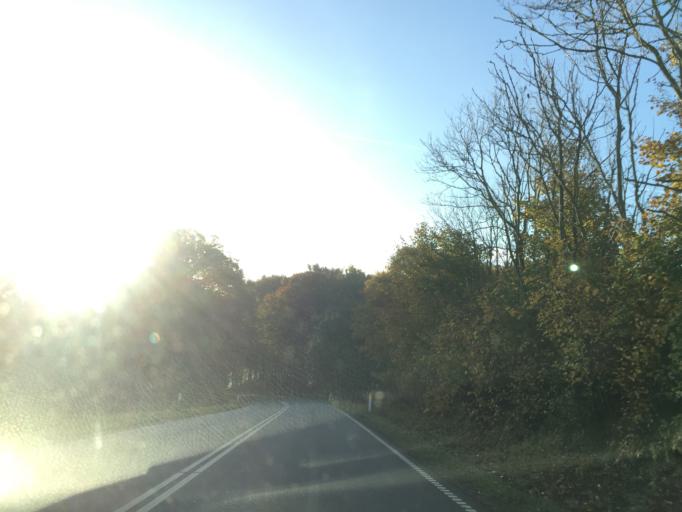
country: DK
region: Central Jutland
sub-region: Skanderborg Kommune
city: Skanderborg
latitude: 56.0616
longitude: 9.9018
